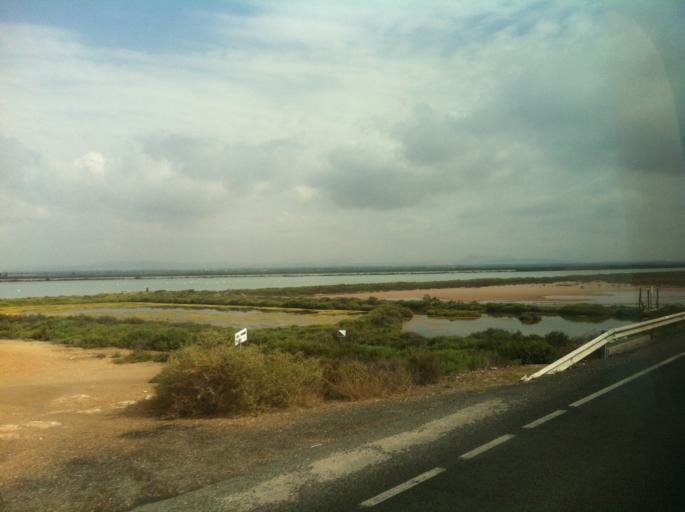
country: ES
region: Valencia
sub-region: Provincia de Alicante
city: Santa Pola
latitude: 38.1691
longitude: -0.6279
